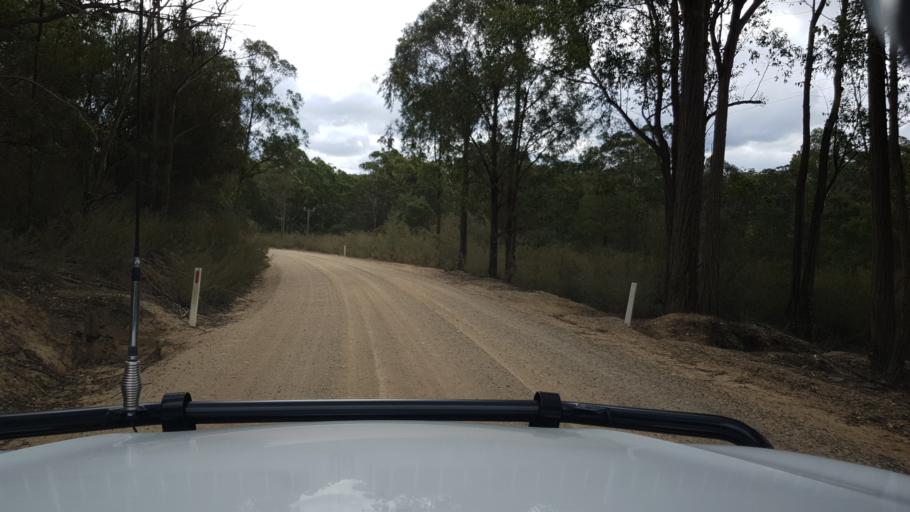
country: AU
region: Victoria
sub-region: East Gippsland
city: Bairnsdale
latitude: -37.6819
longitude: 147.5544
